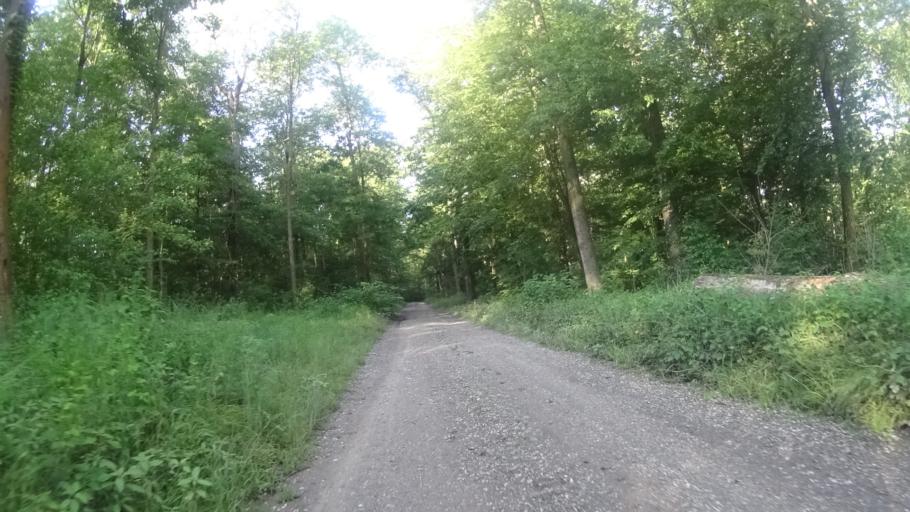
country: DE
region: Baden-Wuerttemberg
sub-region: Freiburg Region
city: Rheinau
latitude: 48.7042
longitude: 7.9583
